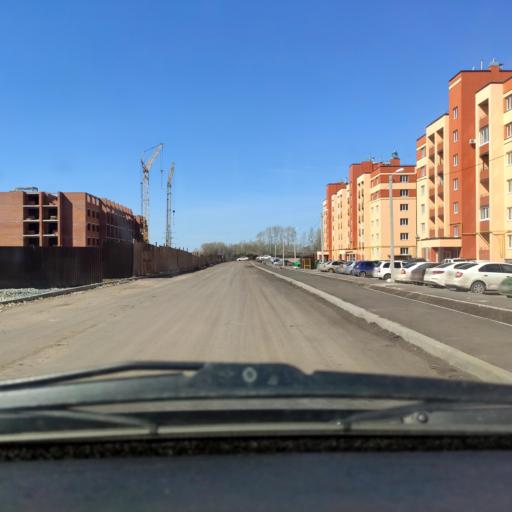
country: RU
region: Bashkortostan
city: Ufa
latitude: 54.6228
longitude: 55.8809
